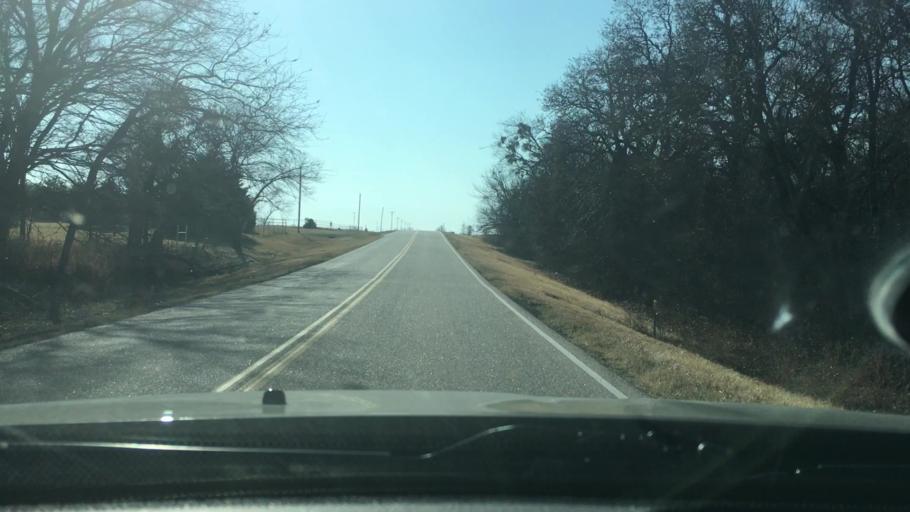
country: US
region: Oklahoma
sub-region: Garvin County
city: Stratford
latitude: 34.8328
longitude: -96.9677
